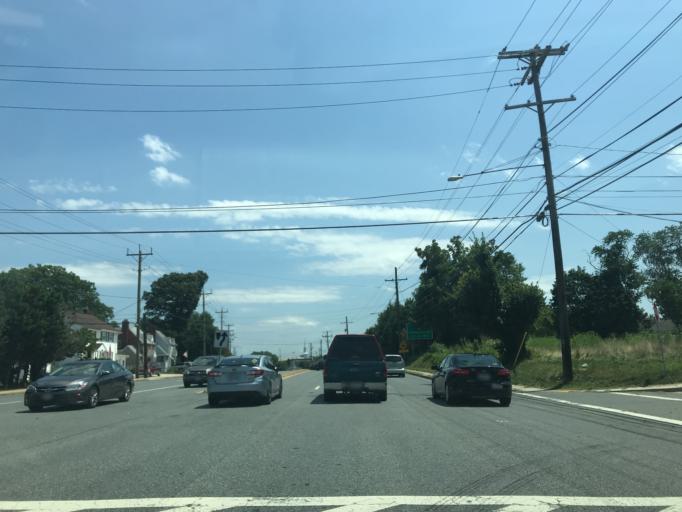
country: US
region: Maryland
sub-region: Montgomery County
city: Four Corners
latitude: 39.0231
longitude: -77.0170
